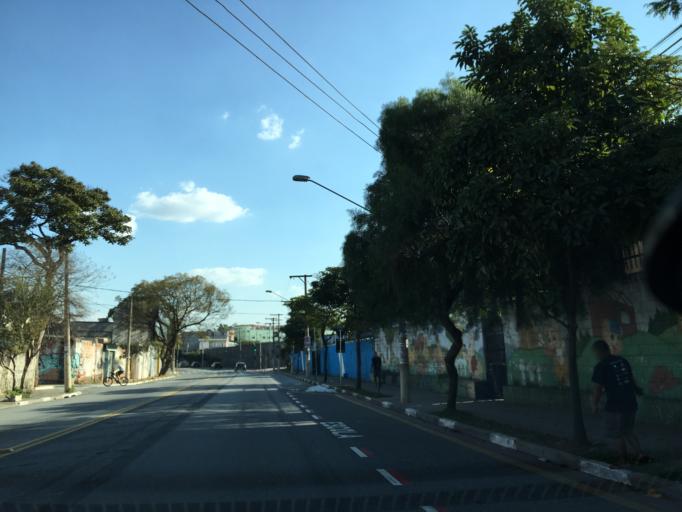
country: BR
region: Sao Paulo
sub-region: Sao Paulo
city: Sao Paulo
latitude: -23.4836
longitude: -46.6496
